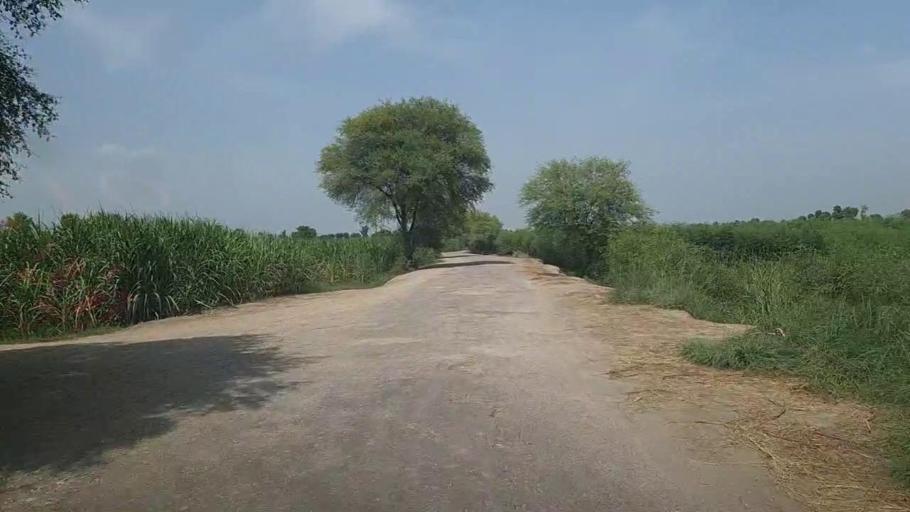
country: PK
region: Sindh
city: Ubauro
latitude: 28.1654
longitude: 69.8301
